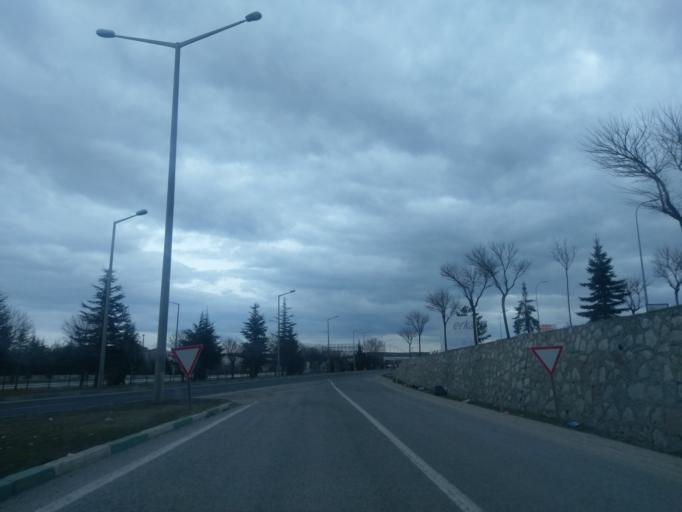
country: TR
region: Kuetahya
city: Kutahya
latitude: 39.3900
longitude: 30.0366
